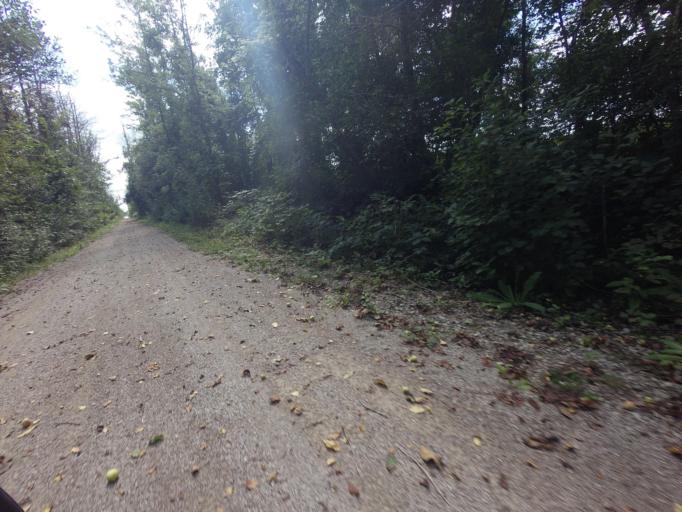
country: CA
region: Ontario
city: Huron East
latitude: 43.6544
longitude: -81.2368
